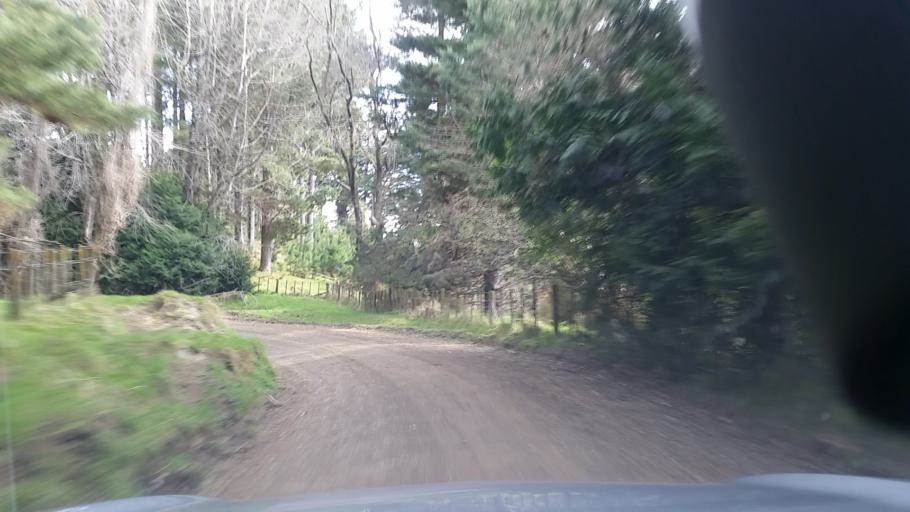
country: NZ
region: Hawke's Bay
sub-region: Napier City
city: Napier
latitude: -39.2296
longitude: 176.9926
